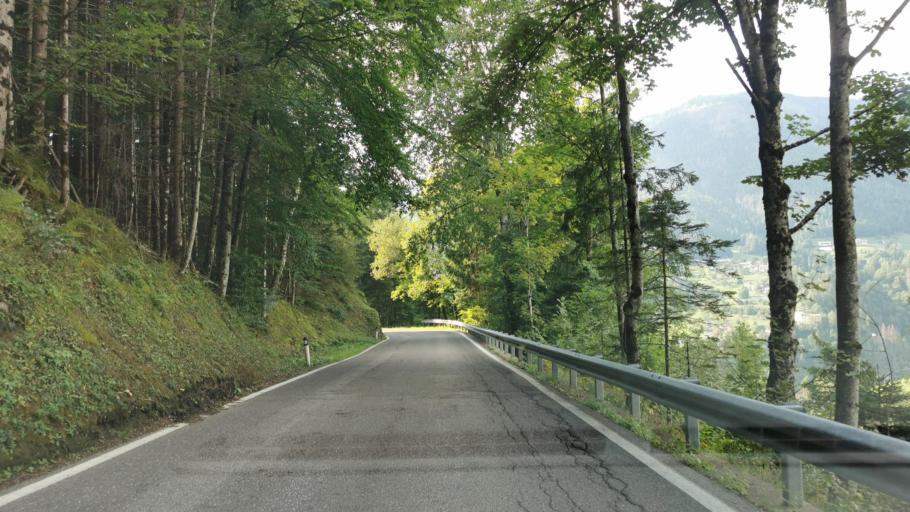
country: IT
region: Trentino-Alto Adige
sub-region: Provincia di Trento
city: Fierozzo
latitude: 46.1060
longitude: 11.3176
